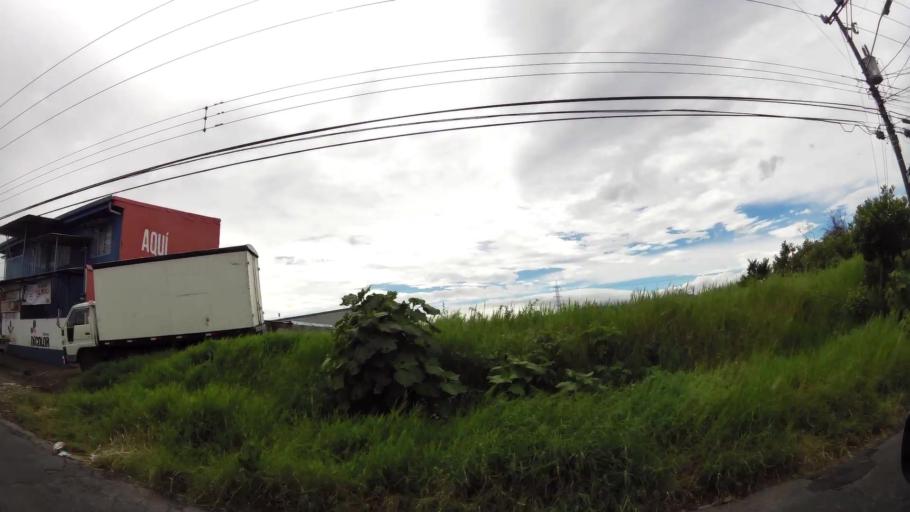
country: CR
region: San Jose
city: Ipis
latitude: 9.9593
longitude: -84.0165
